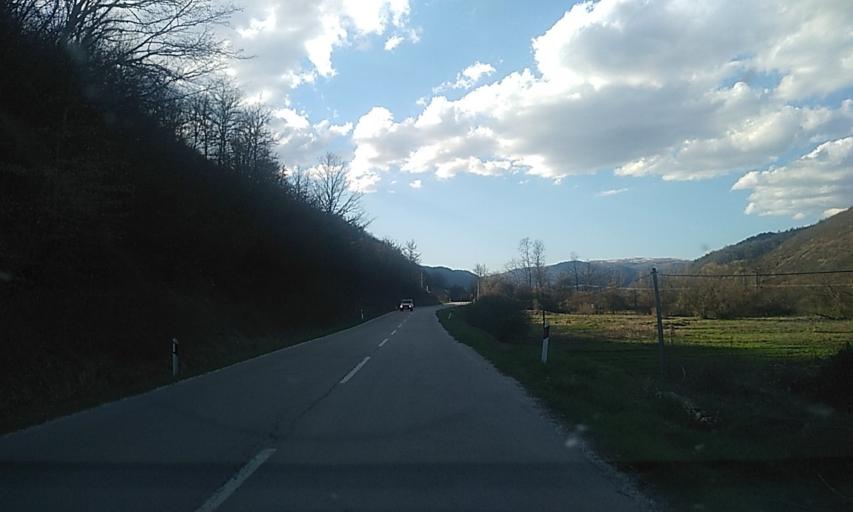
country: RS
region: Central Serbia
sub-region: Pcinjski Okrug
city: Bosilegrad
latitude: 42.4541
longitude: 22.4966
